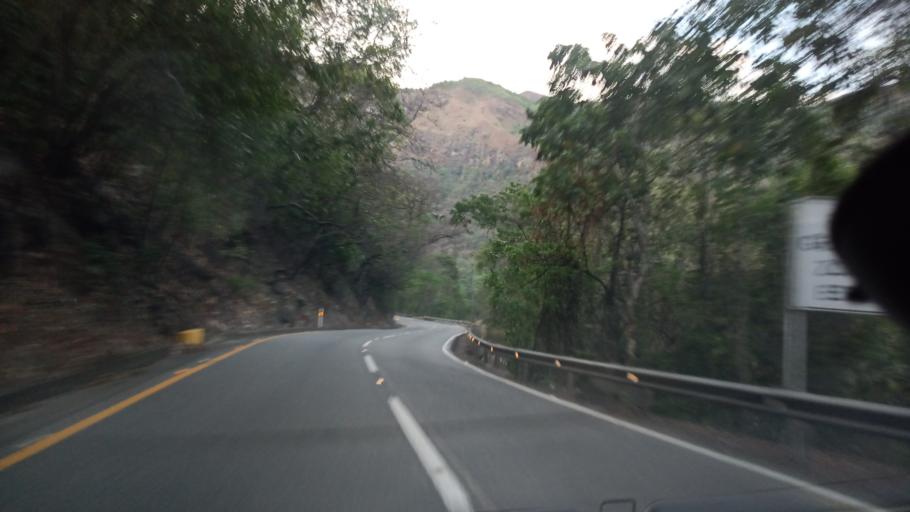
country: CO
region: Cundinamarca
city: Nilo
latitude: 4.2658
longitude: -74.5550
